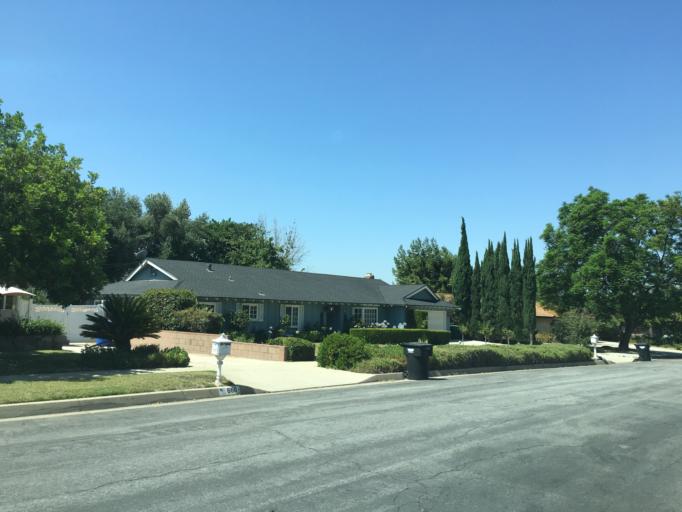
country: US
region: California
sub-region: Los Angeles County
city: La Verne
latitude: 34.1211
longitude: -117.7590
